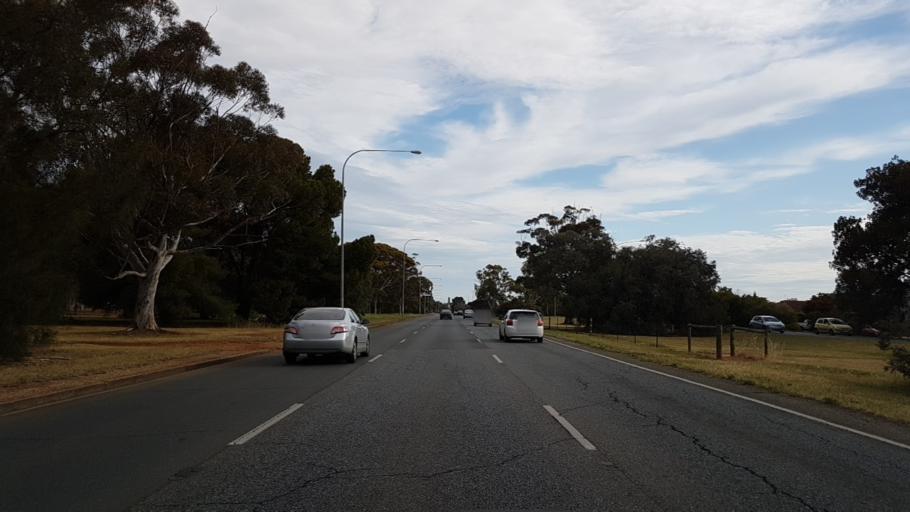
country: AU
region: South Australia
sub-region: Salisbury
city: Elizabeth
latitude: -34.7032
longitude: 138.6813
